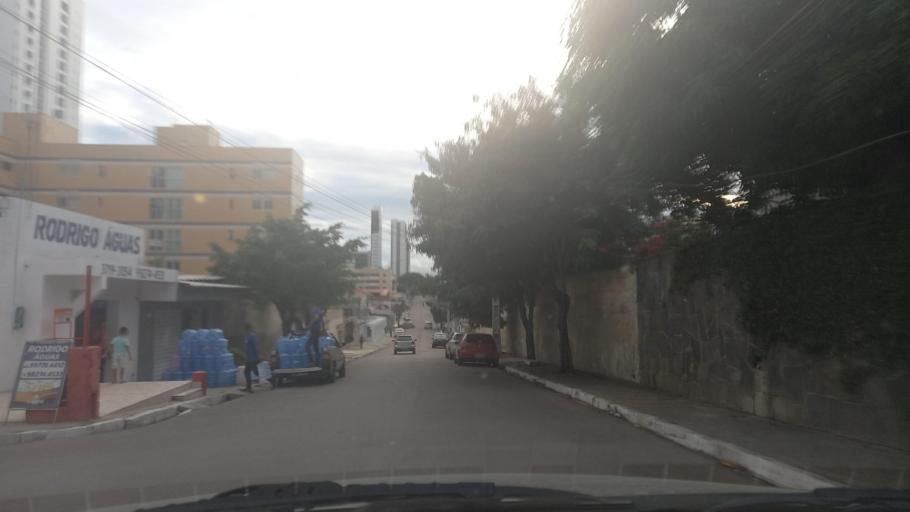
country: BR
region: Pernambuco
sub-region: Caruaru
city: Caruaru
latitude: -8.2699
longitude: -35.9679
